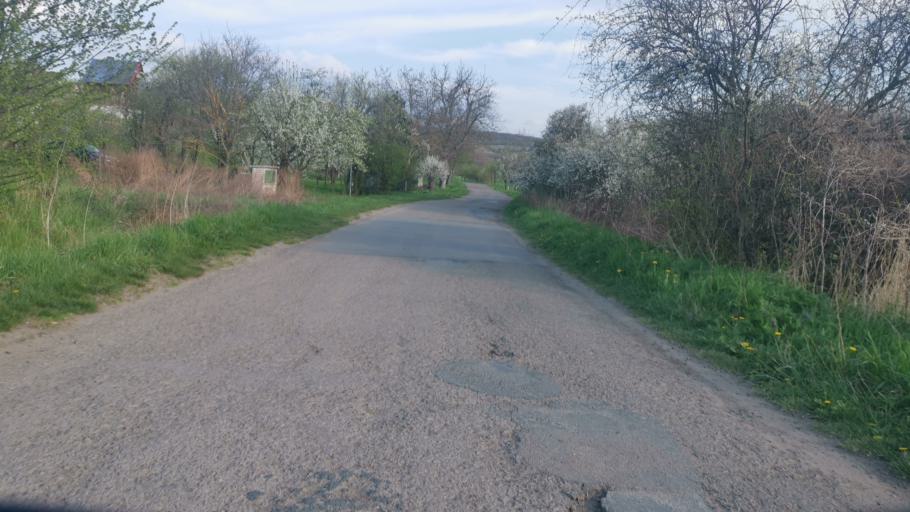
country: CZ
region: South Moravian
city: Petrov
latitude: 48.8494
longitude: 17.3006
